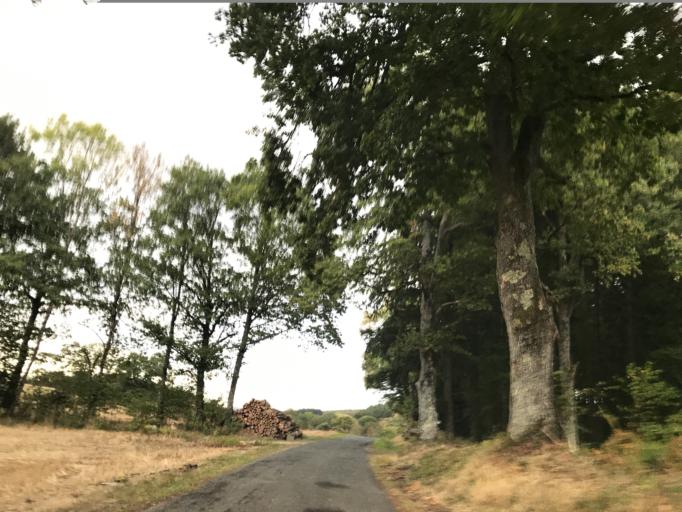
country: FR
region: Auvergne
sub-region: Departement du Puy-de-Dome
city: Thiers
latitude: 45.8400
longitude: 3.5849
